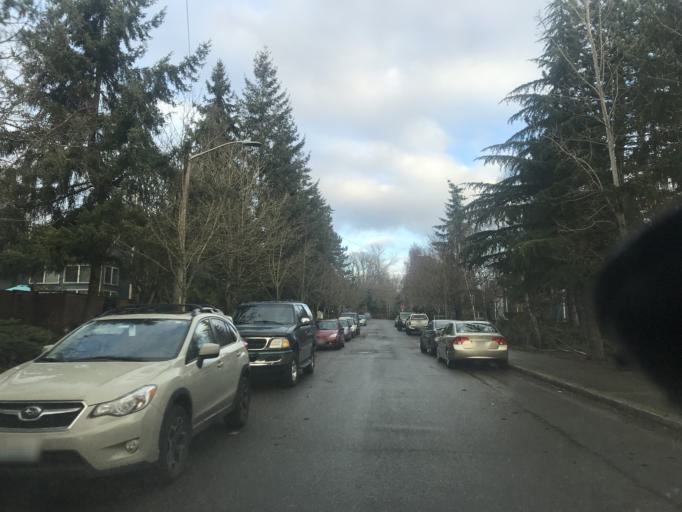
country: US
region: Washington
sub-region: King County
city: White Center
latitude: 47.5271
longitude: -122.3645
